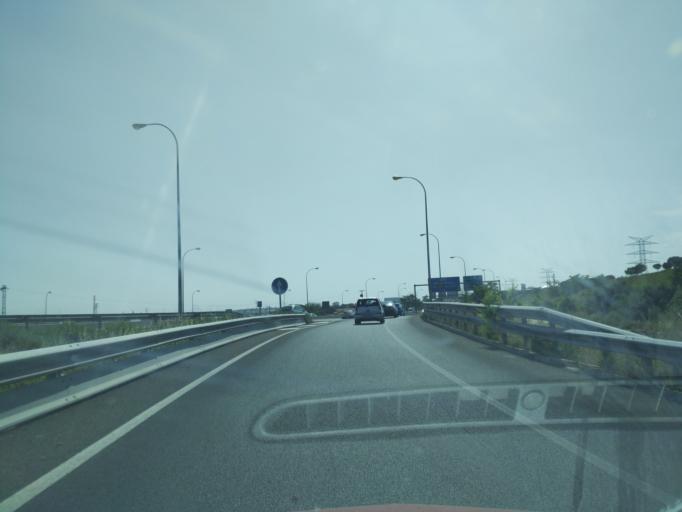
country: ES
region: Madrid
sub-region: Provincia de Madrid
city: Carabanchel
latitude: 40.3650
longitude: -3.7231
